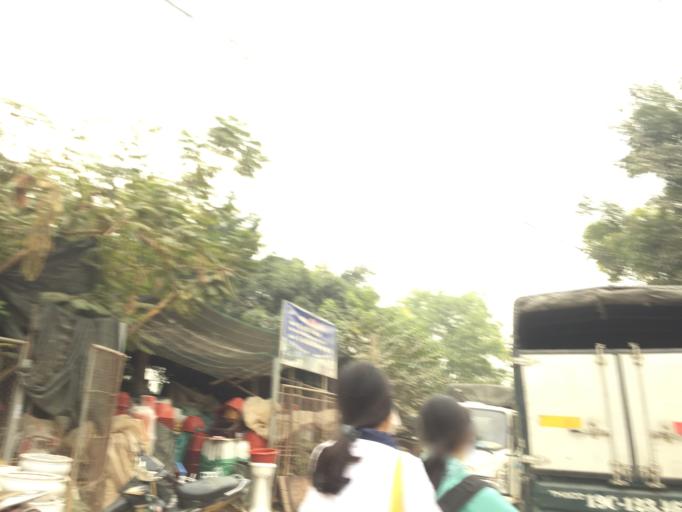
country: VN
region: Hung Yen
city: Van Giang
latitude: 20.9714
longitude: 105.9124
